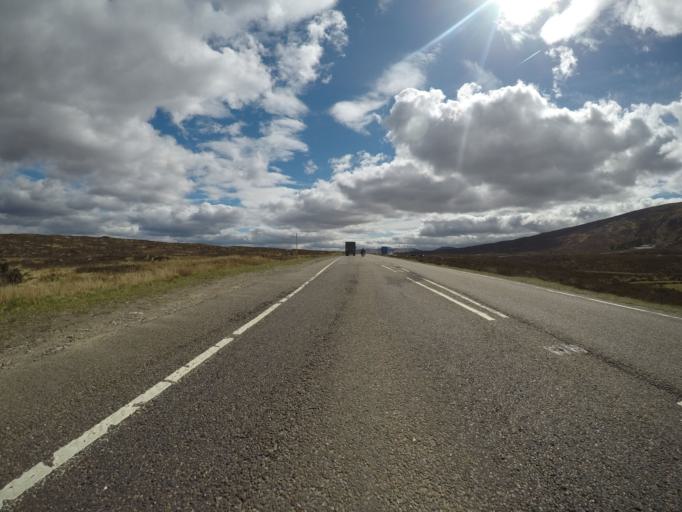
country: GB
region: Scotland
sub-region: Highland
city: Spean Bridge
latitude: 56.6440
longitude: -4.8293
